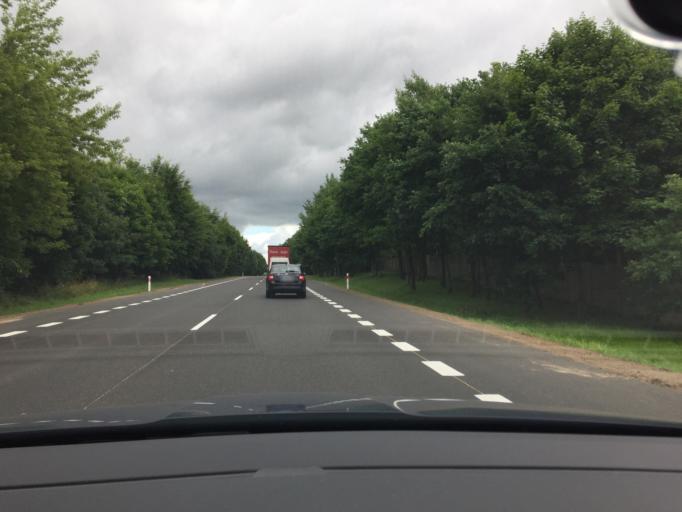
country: PL
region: West Pomeranian Voivodeship
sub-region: Powiat bialogardzki
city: Karlino
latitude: 54.0521
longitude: 15.9120
